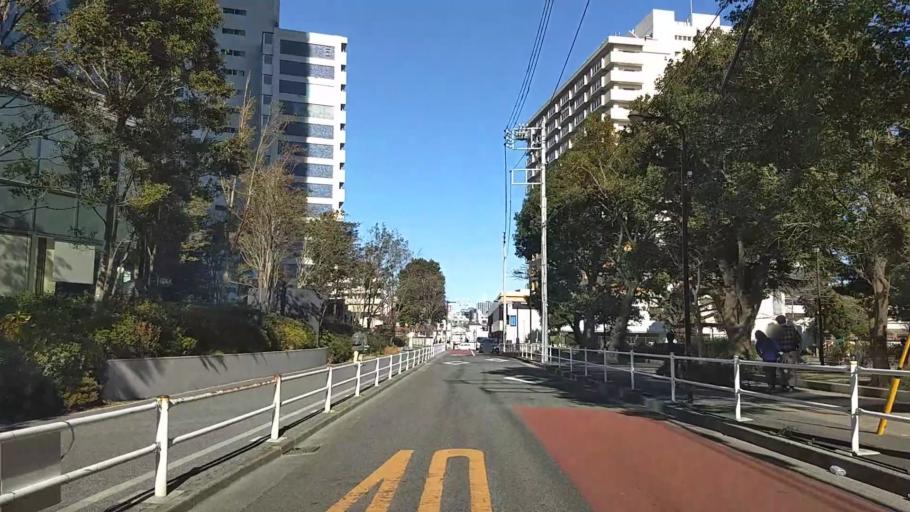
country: JP
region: Tokyo
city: Tokyo
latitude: 35.7072
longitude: 139.7038
